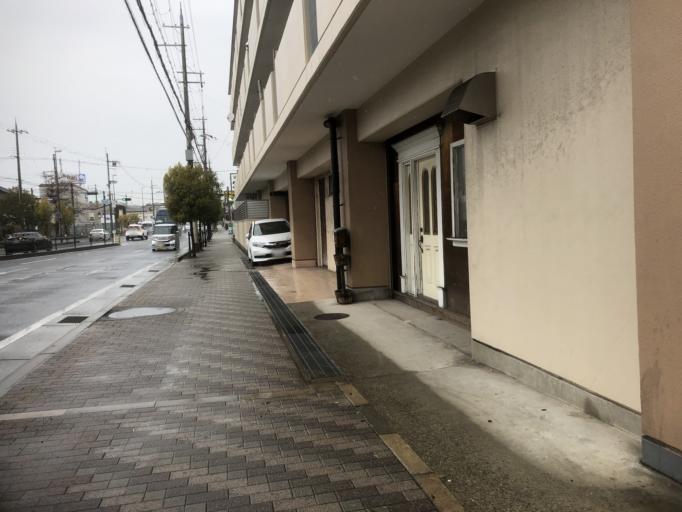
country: JP
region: Hyogo
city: Itami
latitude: 34.7535
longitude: 135.4217
